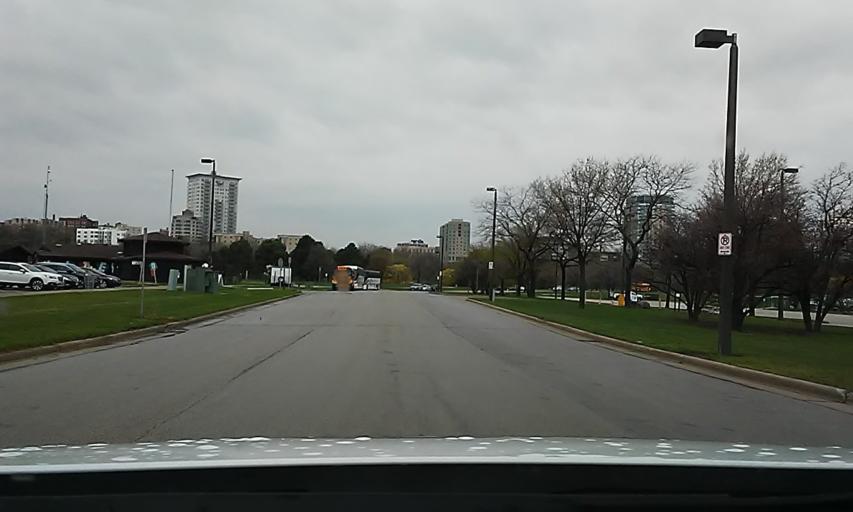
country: US
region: Wisconsin
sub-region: Milwaukee County
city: Milwaukee
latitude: 43.0445
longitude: -87.8889
